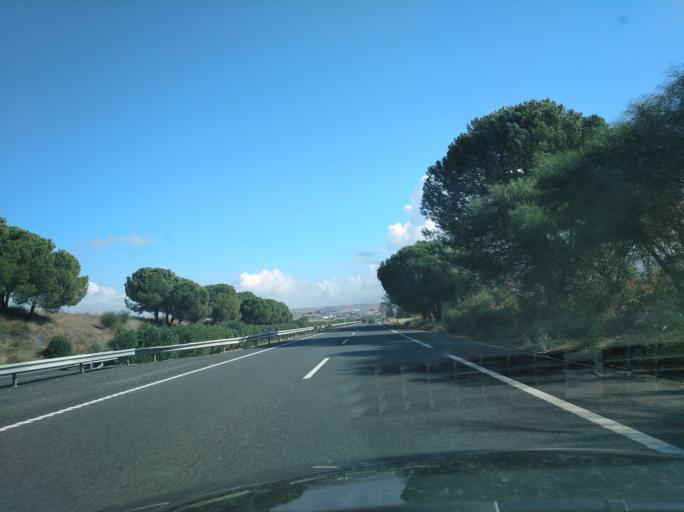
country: ES
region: Andalusia
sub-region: Provincia de Huelva
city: Chucena
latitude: 37.3544
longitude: -6.3612
